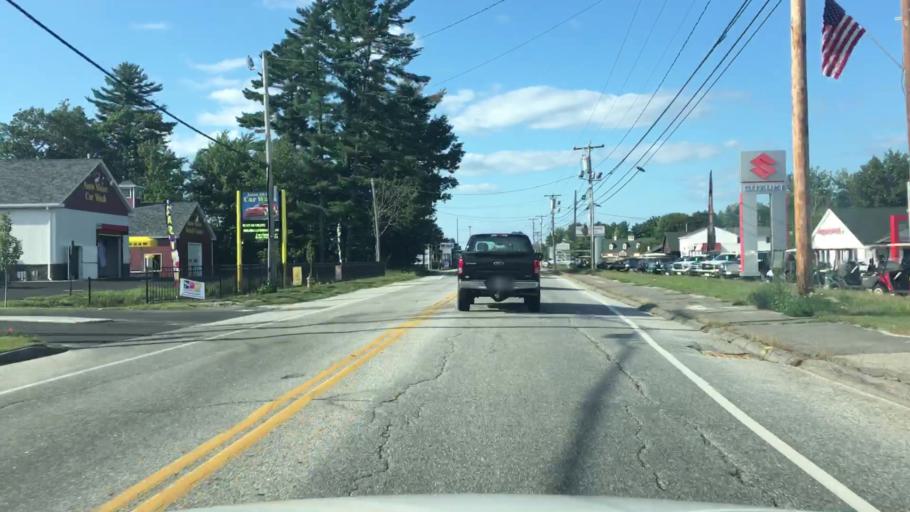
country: US
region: Maine
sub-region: Cumberland County
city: North Windham
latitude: 43.8256
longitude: -70.4345
